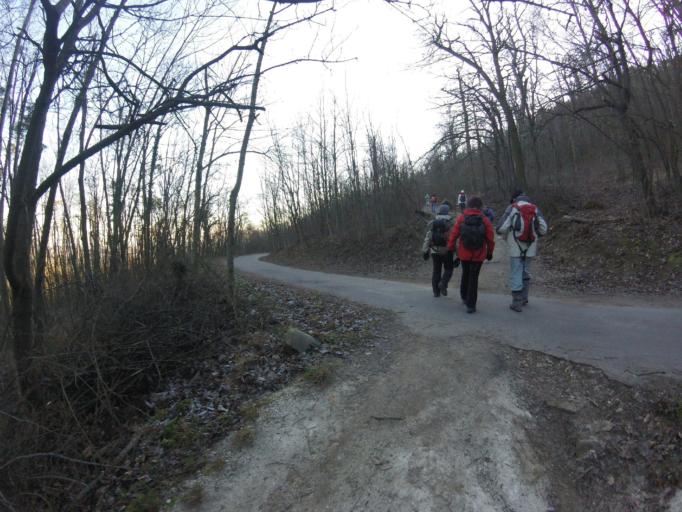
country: HU
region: Pest
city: Budakeszi
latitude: 47.5224
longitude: 18.9581
